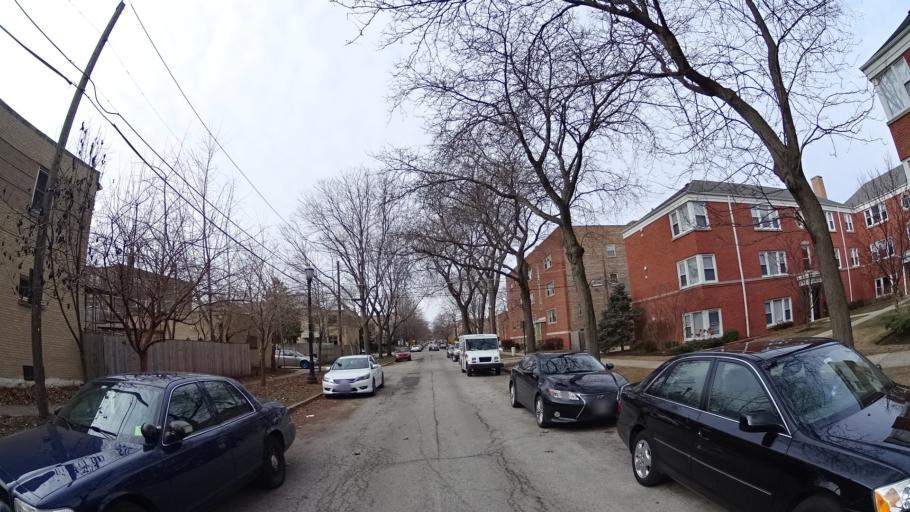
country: US
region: Illinois
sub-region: Cook County
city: Evanston
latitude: 42.0212
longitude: -87.6795
